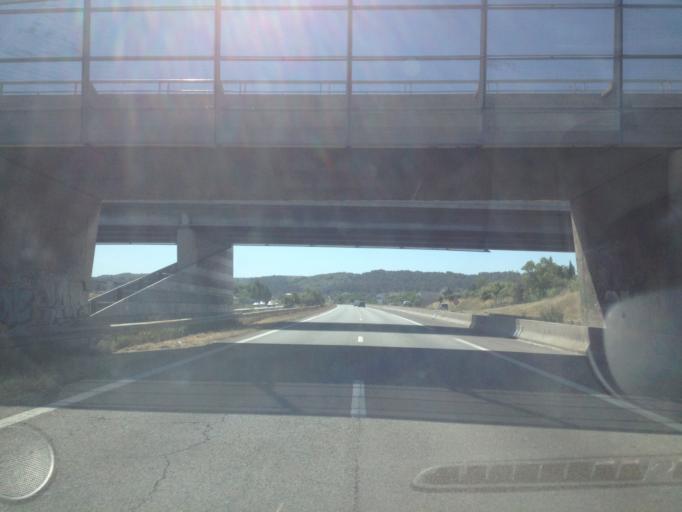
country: FR
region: Provence-Alpes-Cote d'Azur
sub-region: Departement des Bouches-du-Rhone
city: Saint-Victoret
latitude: 43.4217
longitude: 5.2684
